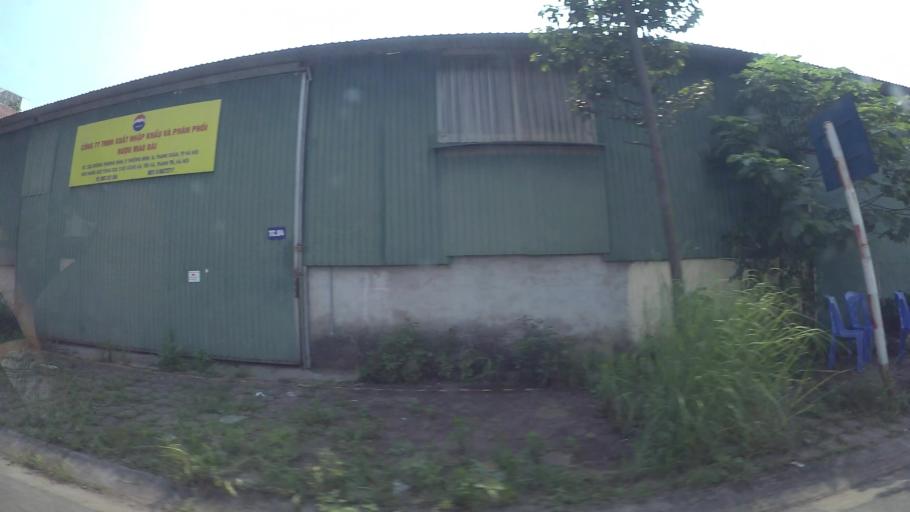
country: VN
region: Ha Noi
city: Ha Dong
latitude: 20.9673
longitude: 105.7992
